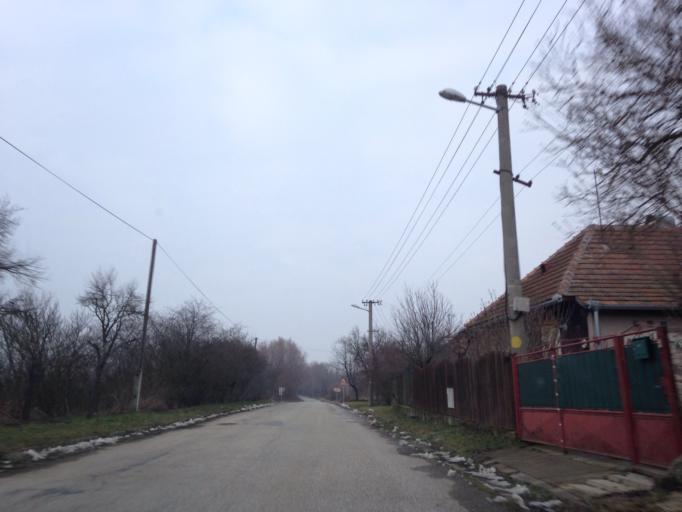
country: SK
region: Nitriansky
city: Svodin
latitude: 48.0381
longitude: 18.3727
